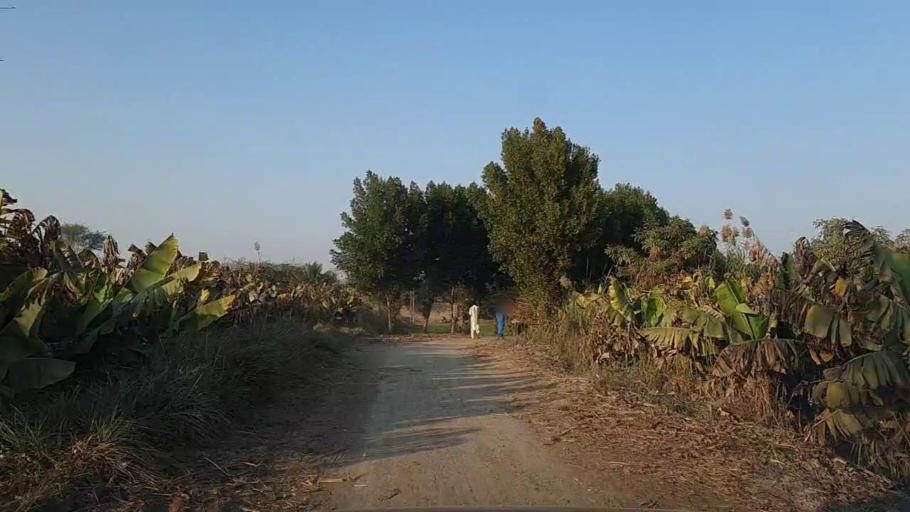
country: PK
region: Sindh
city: Daur
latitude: 26.4663
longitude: 68.3880
